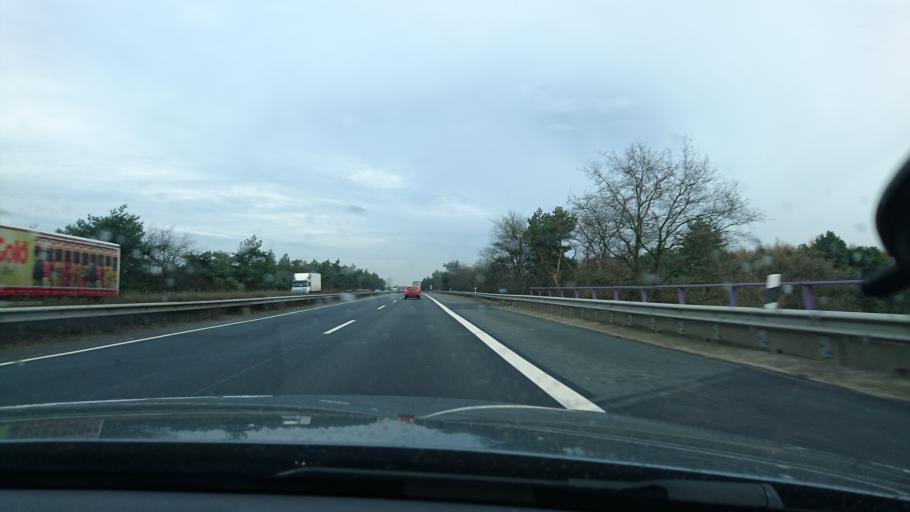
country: DE
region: Lower Saxony
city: Holdorf
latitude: 52.5605
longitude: 8.1130
